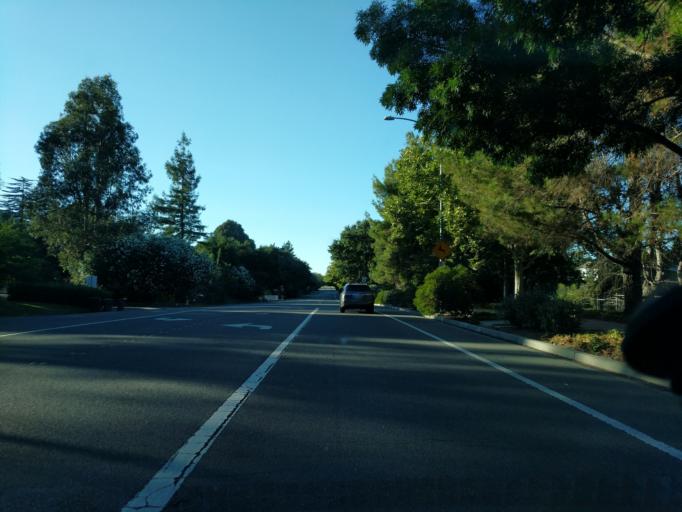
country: US
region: California
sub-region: Alameda County
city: Pleasanton
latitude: 37.6546
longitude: -121.9080
